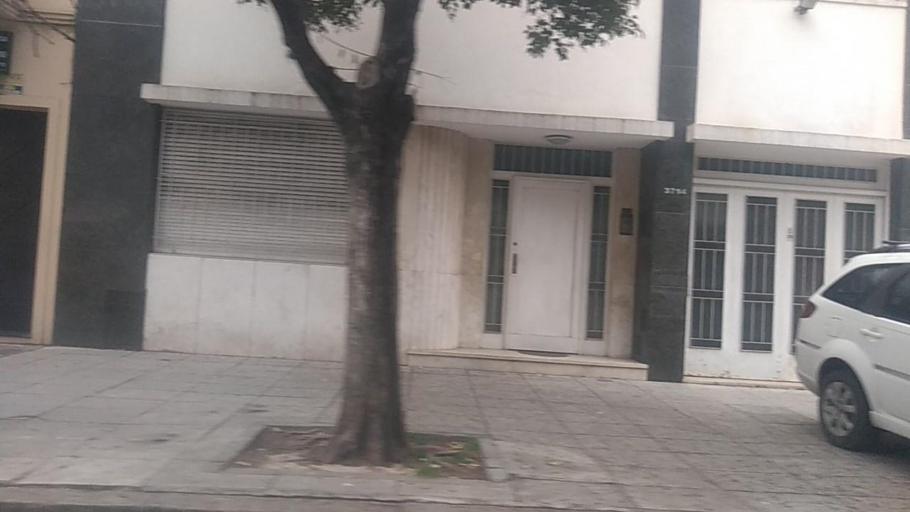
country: AR
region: Buenos Aires F.D.
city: Villa Santa Rita
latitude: -34.6039
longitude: -58.5014
